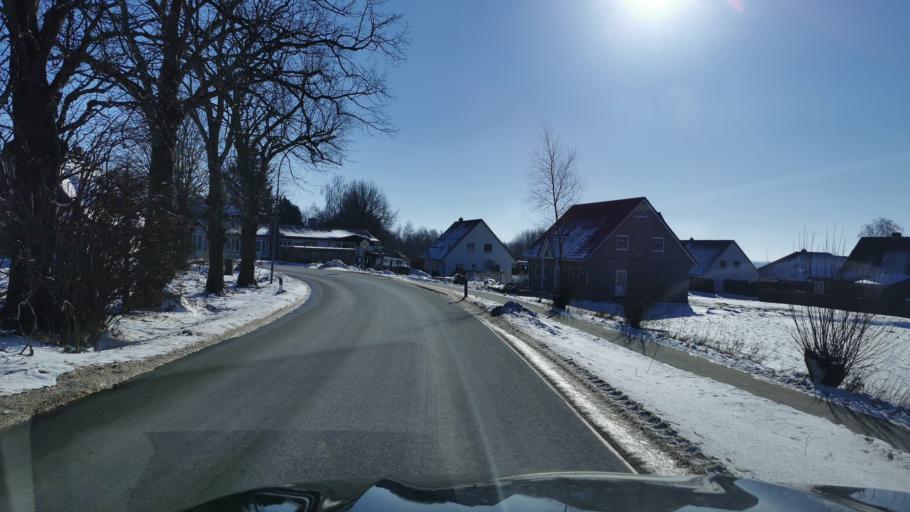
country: DE
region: Schleswig-Holstein
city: Sorup
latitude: 54.7272
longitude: 9.6550
